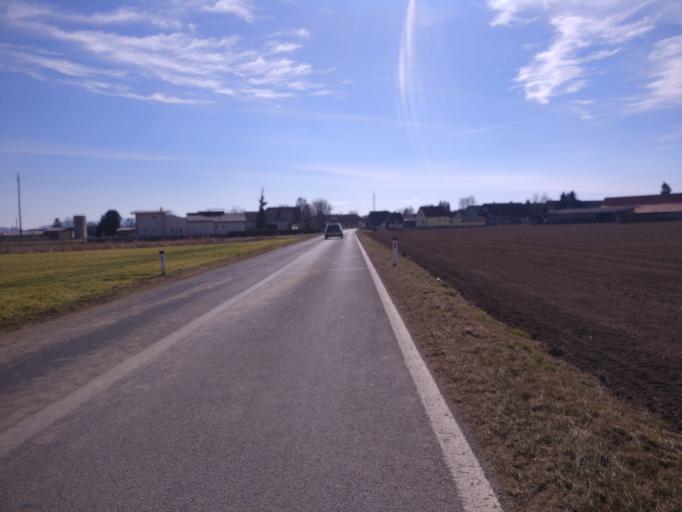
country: AT
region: Styria
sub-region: Politischer Bezirk Graz-Umgebung
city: Wundschuh
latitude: 46.9496
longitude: 15.4437
